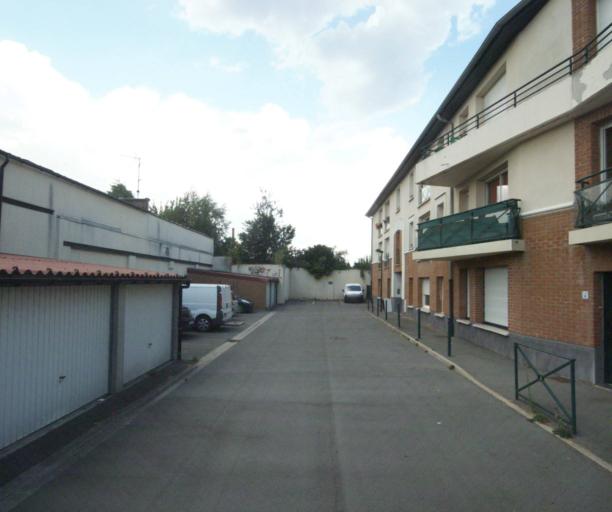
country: FR
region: Nord-Pas-de-Calais
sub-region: Departement du Nord
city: Deulemont
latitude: 50.7354
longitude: 2.9459
